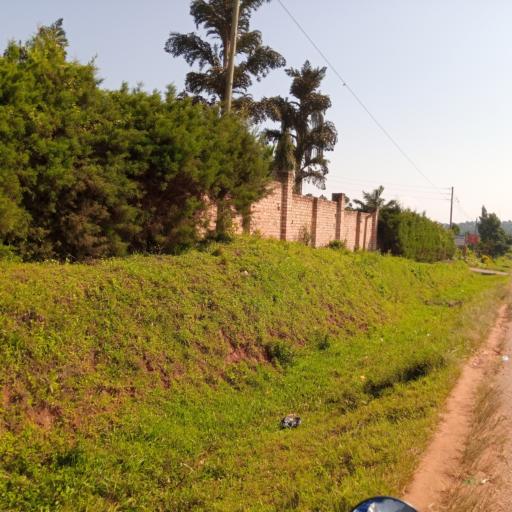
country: UG
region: Central Region
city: Masaka
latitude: -0.3581
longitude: 31.7208
